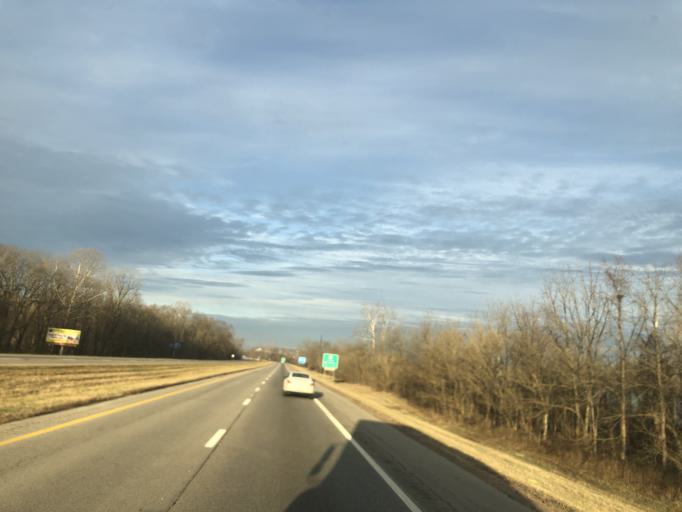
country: US
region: Ohio
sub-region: Hocking County
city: Logan
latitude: 39.5309
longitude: -82.3932
